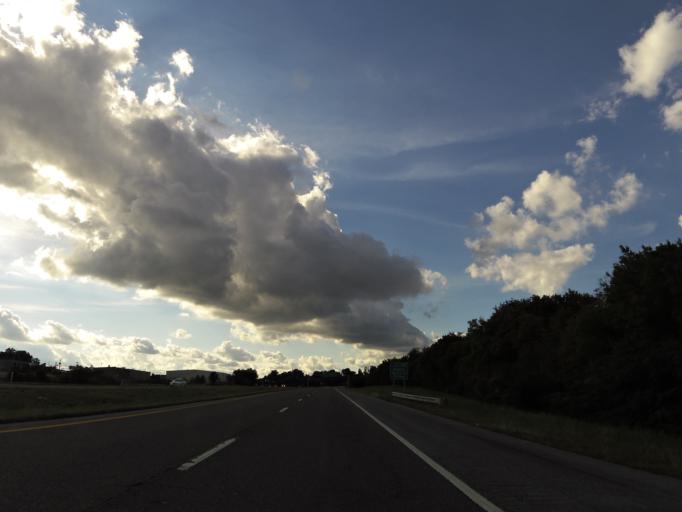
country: US
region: Tennessee
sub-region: Blount County
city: Alcoa
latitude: 35.8316
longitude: -83.9639
